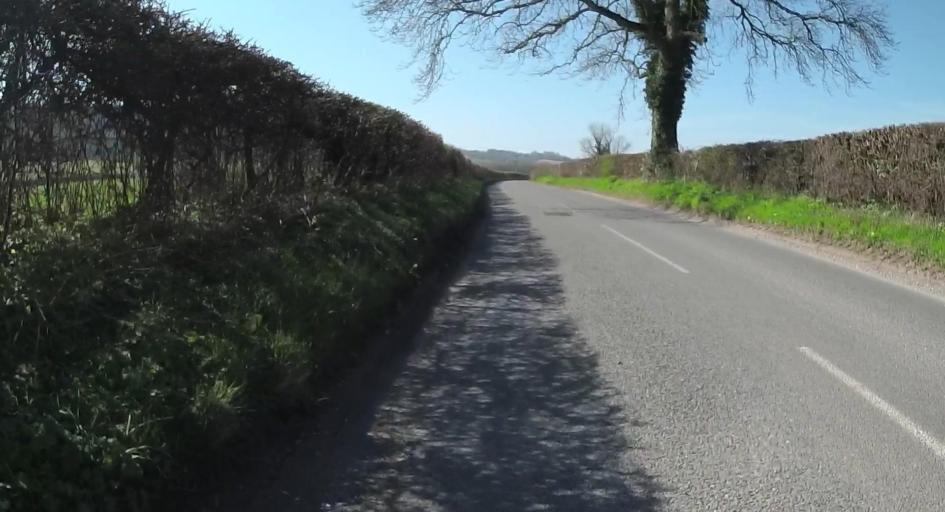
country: GB
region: England
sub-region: Hampshire
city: Andover
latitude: 51.2682
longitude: -1.4312
